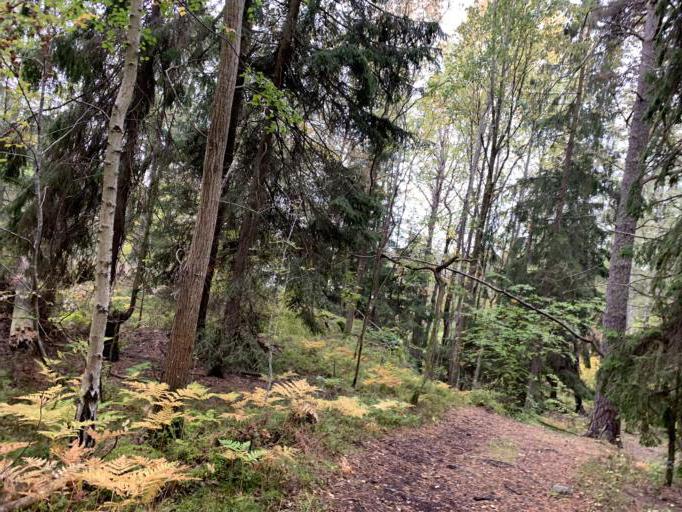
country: SE
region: Stockholm
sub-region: Lidingo
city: Brevik
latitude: 59.3593
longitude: 18.1693
